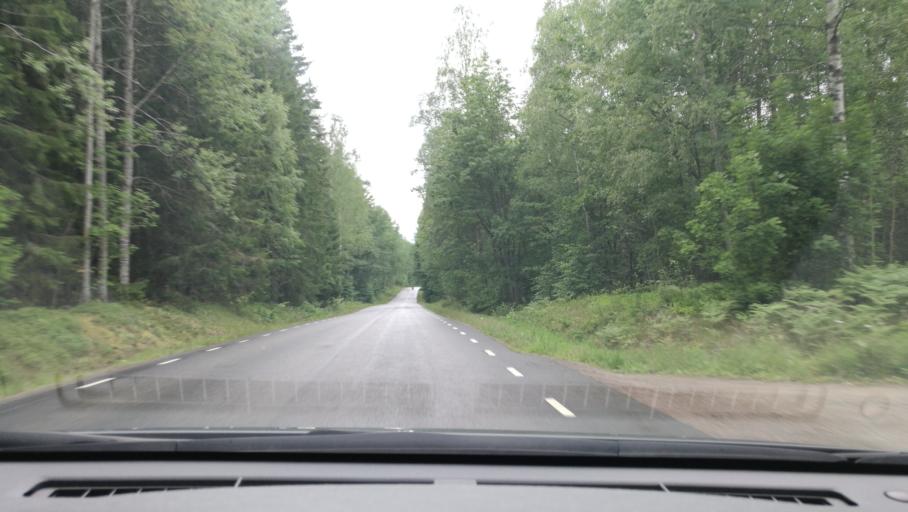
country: SE
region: OEstergoetland
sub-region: Norrkopings Kommun
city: Svartinge
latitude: 58.8237
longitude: 15.9799
